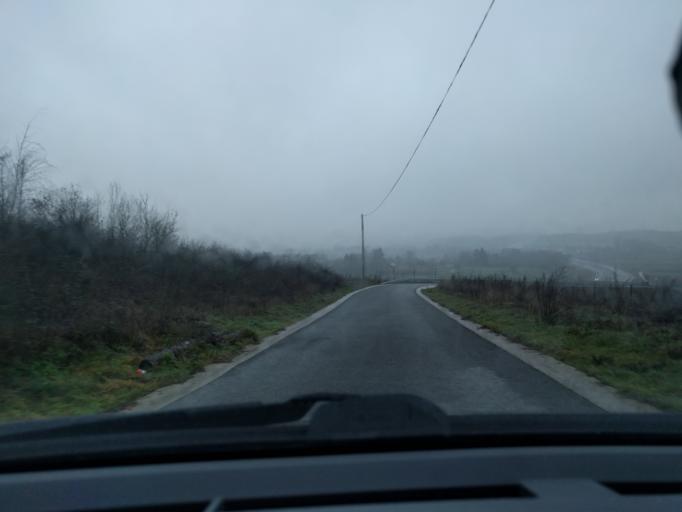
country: BE
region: Wallonia
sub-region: Province de Namur
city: Couvin
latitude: 50.0445
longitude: 4.5133
